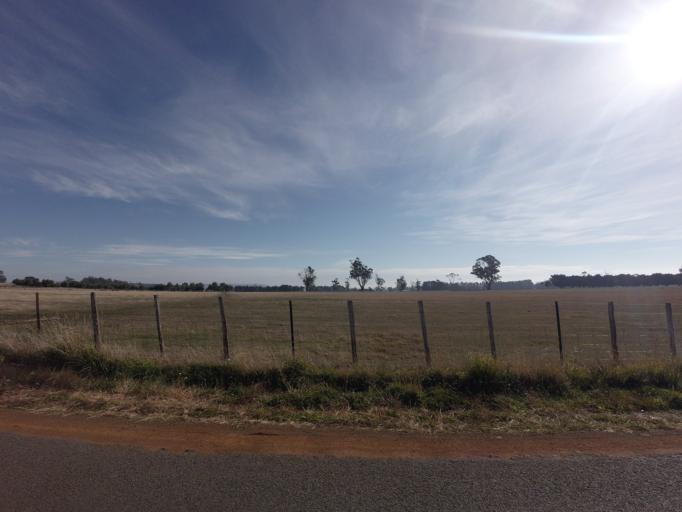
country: AU
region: Tasmania
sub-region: Sorell
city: Sorell
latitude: -42.4506
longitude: 147.4620
